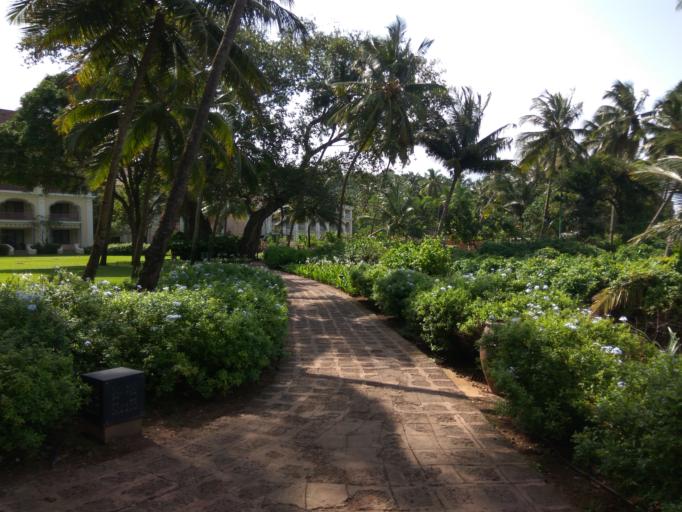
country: IN
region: Goa
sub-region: North Goa
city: Bambolim
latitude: 15.4499
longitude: 73.8520
